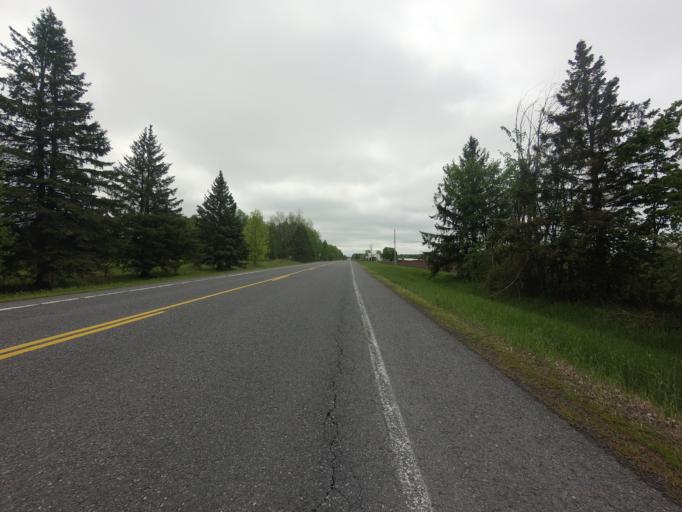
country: CA
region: Ontario
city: Casselman
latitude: 45.0501
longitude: -75.1989
